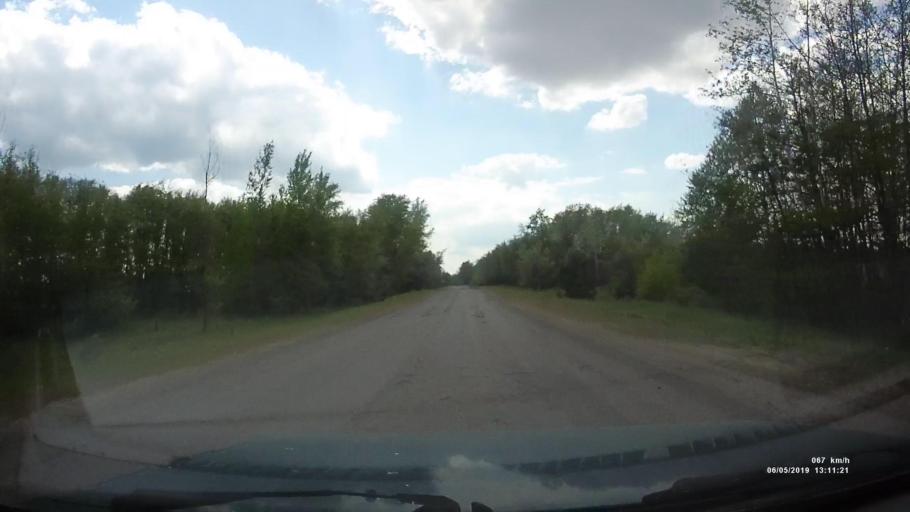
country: RU
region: Rostov
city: Ust'-Donetskiy
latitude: 47.7561
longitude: 40.9590
